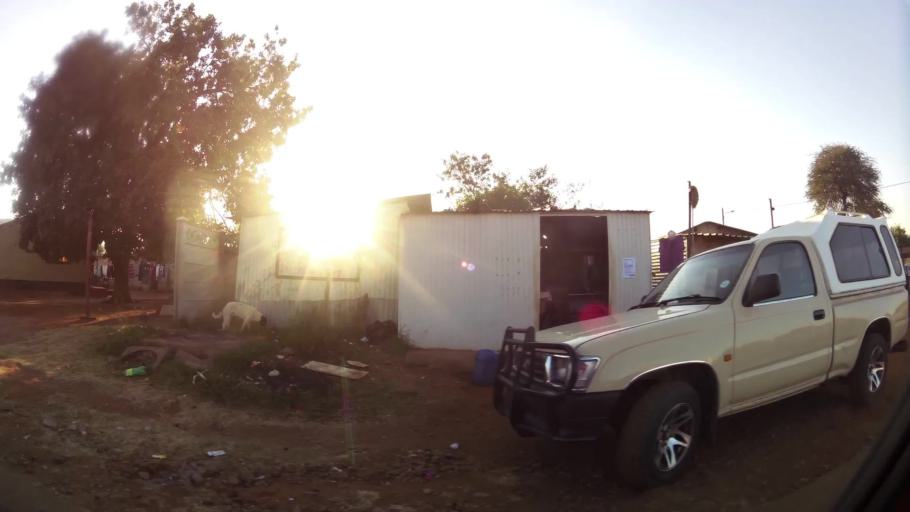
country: ZA
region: North-West
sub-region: Bojanala Platinum District Municipality
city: Rustenburg
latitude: -25.6364
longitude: 27.2112
